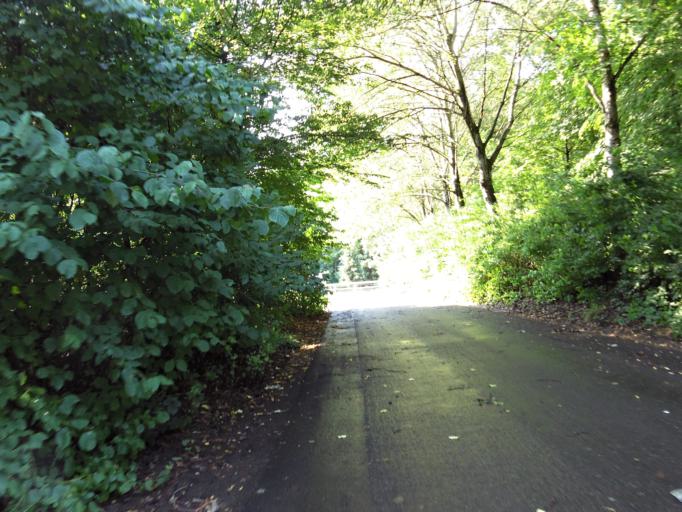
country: NL
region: Limburg
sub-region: Gemeente Kerkrade
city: Kerkrade
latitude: 50.8716
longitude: 6.0245
